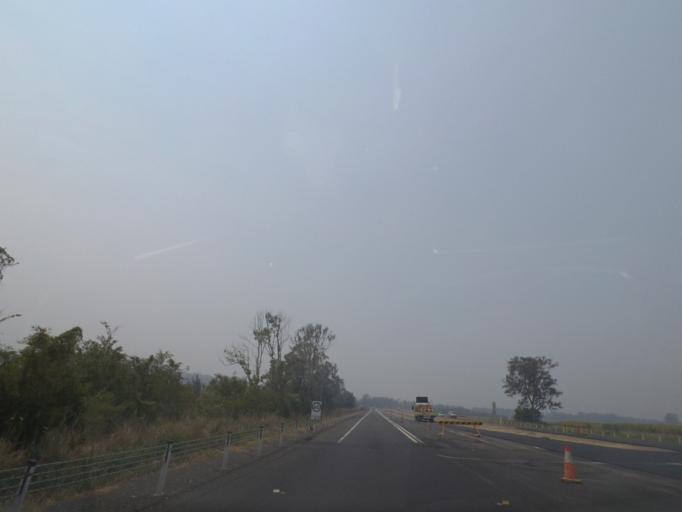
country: AU
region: New South Wales
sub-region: Ballina
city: Ballina
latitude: -28.8739
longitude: 153.4896
